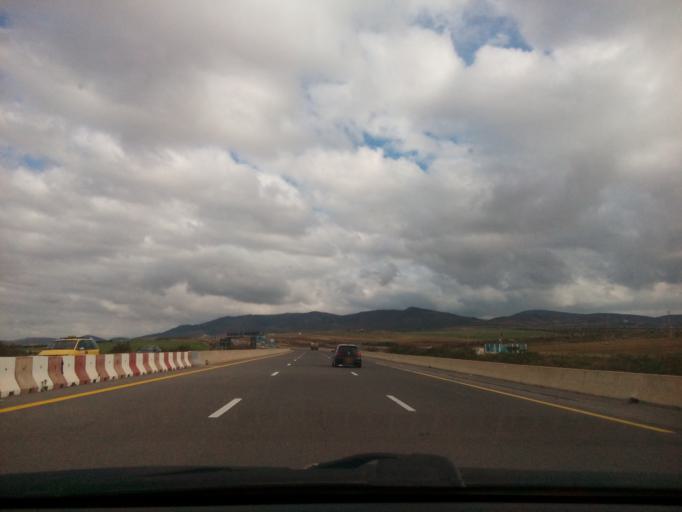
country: DZ
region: Tlemcen
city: Bensekrane
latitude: 34.9873
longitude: -1.2221
